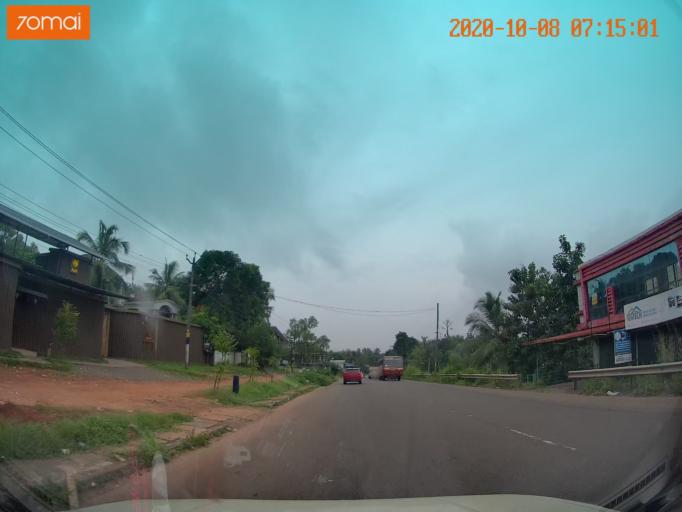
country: IN
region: Kerala
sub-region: Malappuram
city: Ponnani
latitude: 10.8225
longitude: 76.0179
